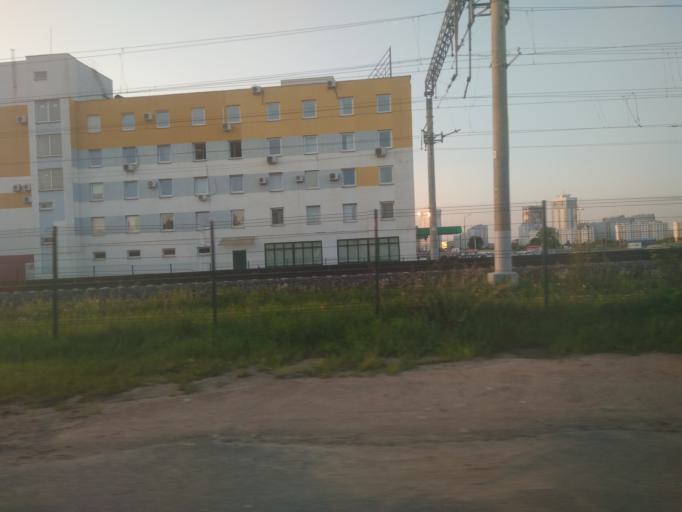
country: BY
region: Minsk
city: Zhdanovichy
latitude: 53.9314
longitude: 27.4604
